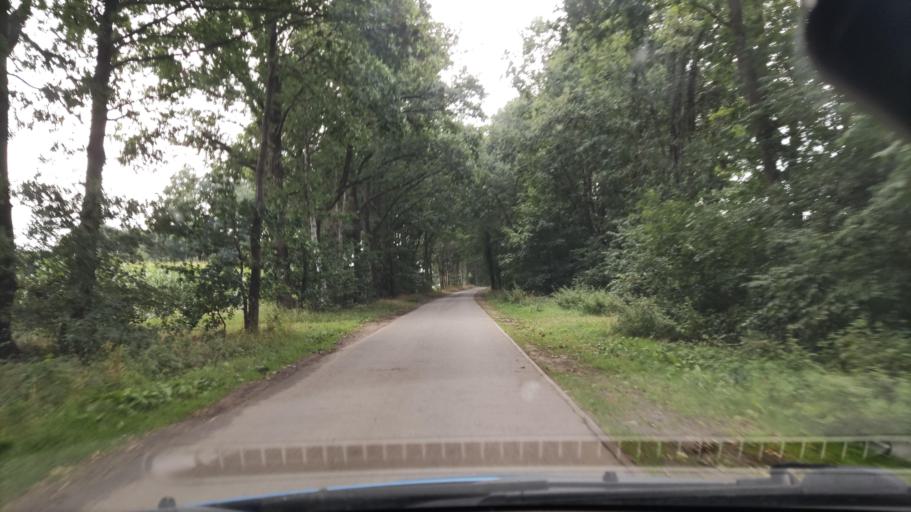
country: DE
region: Lower Saxony
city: Wittorf
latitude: 53.3439
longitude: 10.3741
